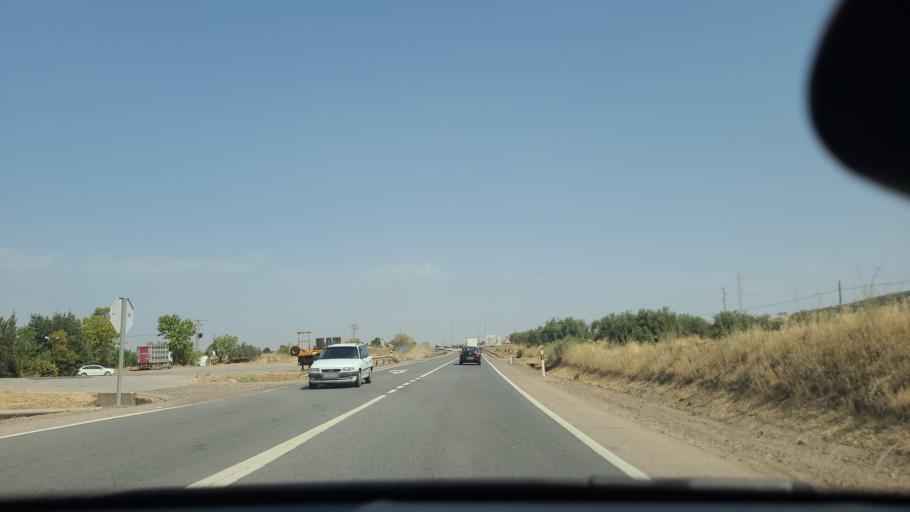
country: ES
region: Extremadura
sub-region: Provincia de Badajoz
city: Zafra
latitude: 38.4365
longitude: -6.4235
